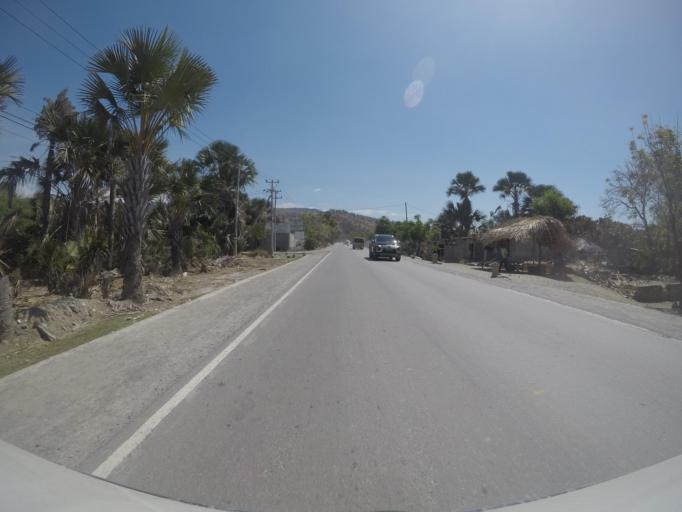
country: TL
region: Dili
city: Dili
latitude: -8.5725
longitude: 125.4613
